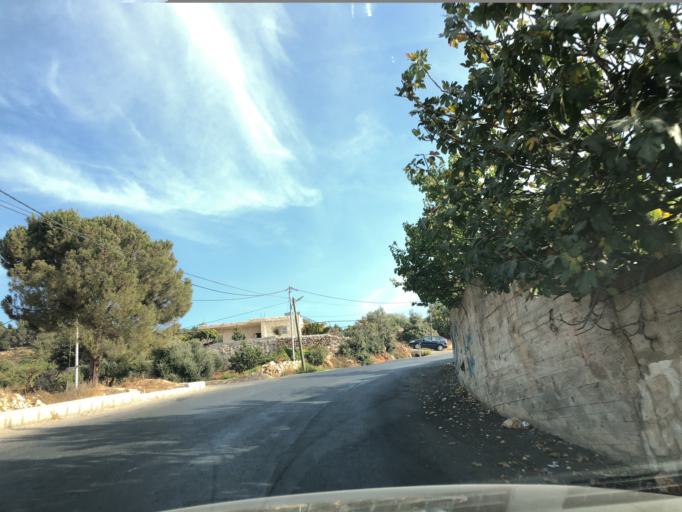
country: JO
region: Irbid
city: `Ayn Jannah
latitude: 32.3279
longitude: 35.7604
